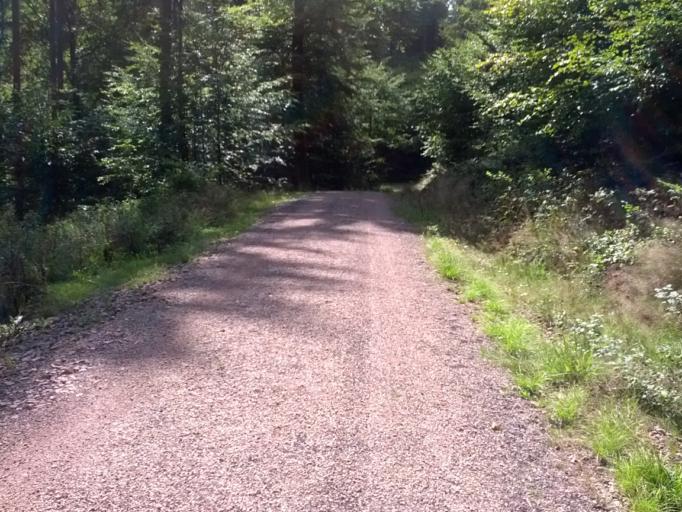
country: DE
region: Thuringia
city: Wolfsburg-Unkeroda
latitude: 50.9411
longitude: 10.3033
